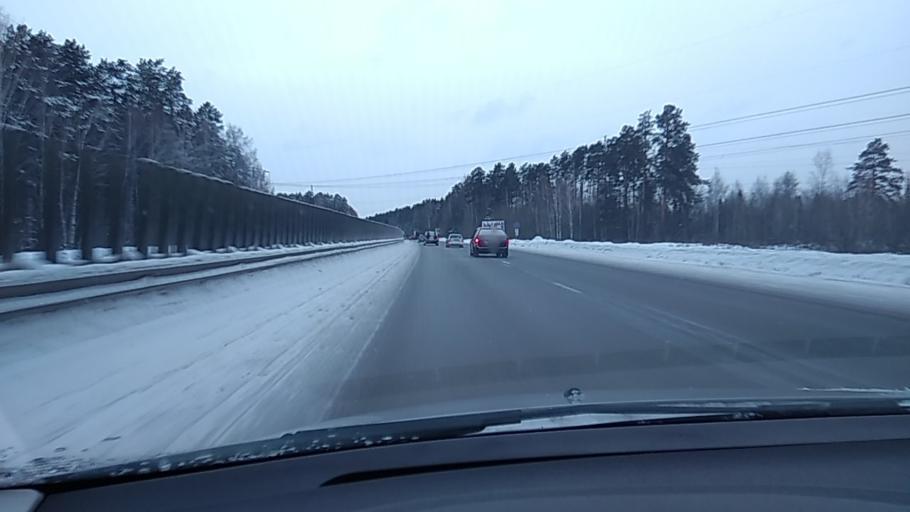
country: RU
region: Sverdlovsk
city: Istok
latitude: 56.7936
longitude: 60.8240
